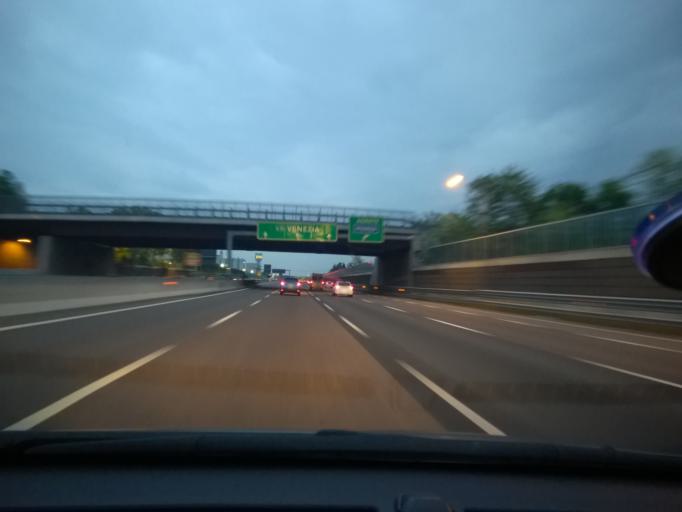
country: IT
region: Lombardy
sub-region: Provincia di Monza e Brianza
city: Agrate Brianza
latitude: 45.5678
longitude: 9.3476
